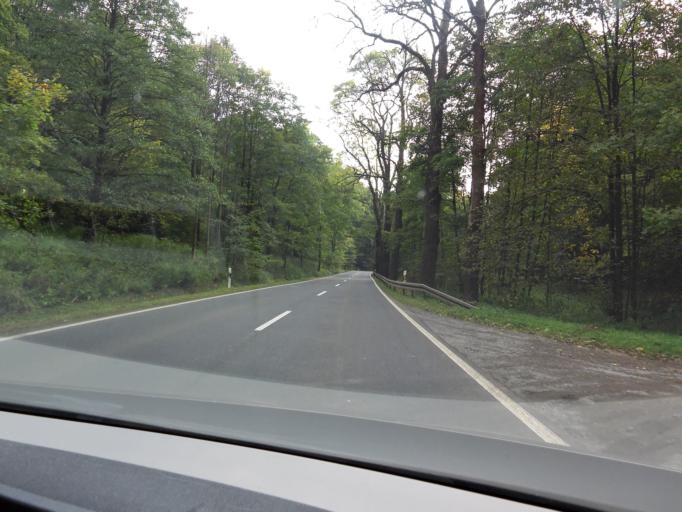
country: DE
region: Thuringia
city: Brotterode
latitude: 50.8129
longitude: 10.4307
